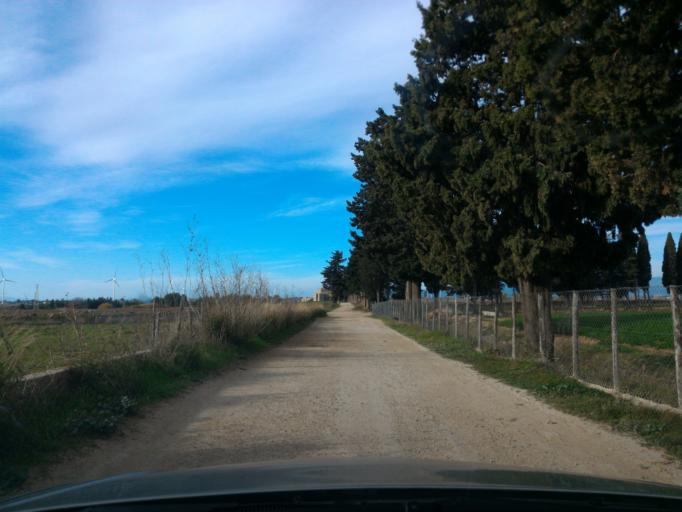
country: IT
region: Calabria
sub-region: Provincia di Crotone
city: Isola di Capo Rizzuto
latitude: 38.9874
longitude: 17.0719
